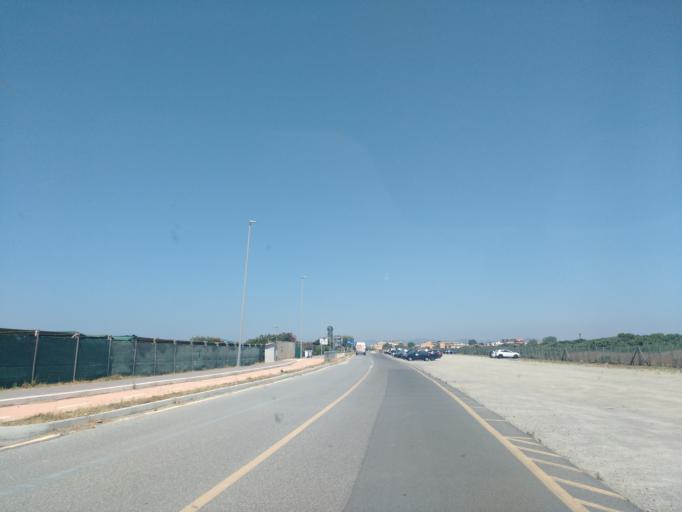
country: IT
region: Latium
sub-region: Citta metropolitana di Roma Capitale
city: Passo Oscuro
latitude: 41.8909
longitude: 12.1662
